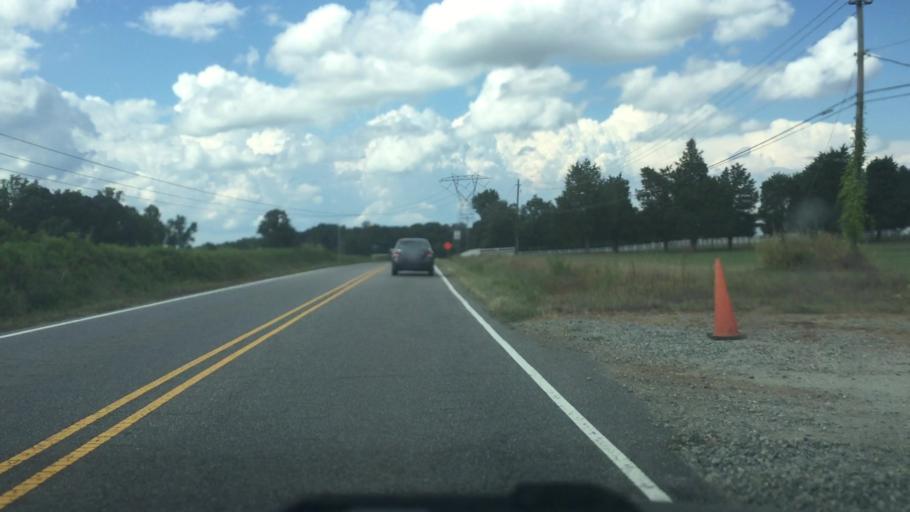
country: US
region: North Carolina
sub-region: Iredell County
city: Mooresville
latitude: 35.5365
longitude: -80.7689
